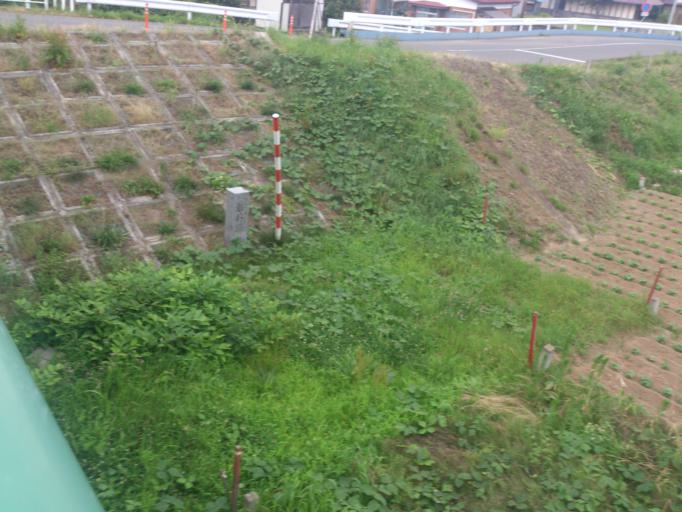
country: JP
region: Iwate
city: Ichinoseki
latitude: 38.9260
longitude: 141.1183
